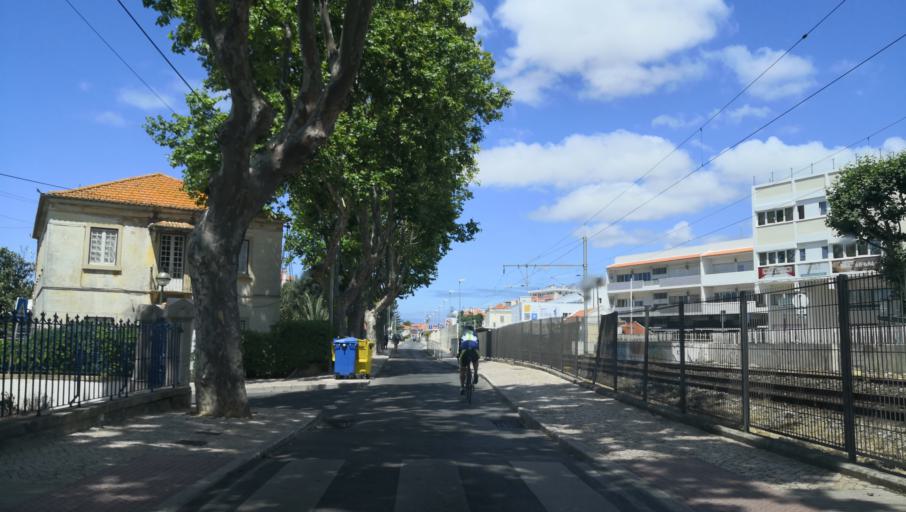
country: PT
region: Lisbon
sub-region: Cascais
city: Parede
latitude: 38.6889
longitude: -9.3542
